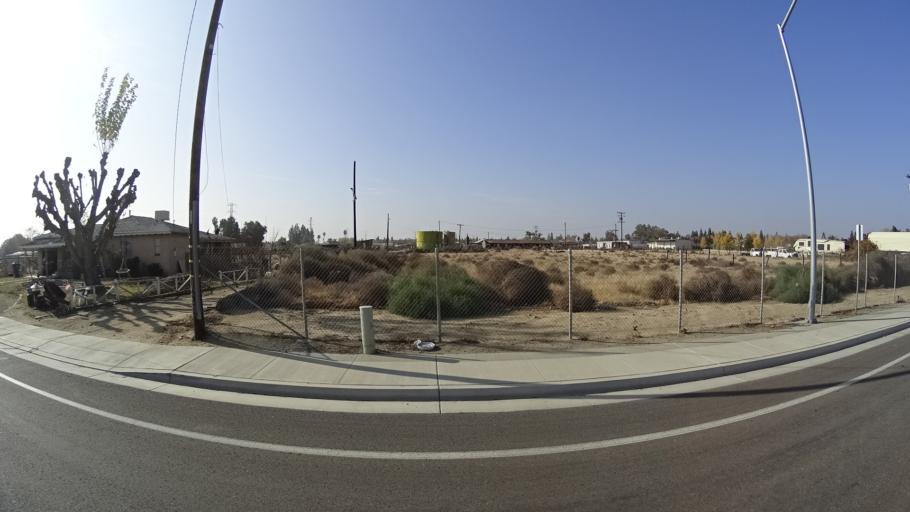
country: US
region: California
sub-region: Kern County
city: Greenacres
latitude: 35.3992
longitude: -119.0655
